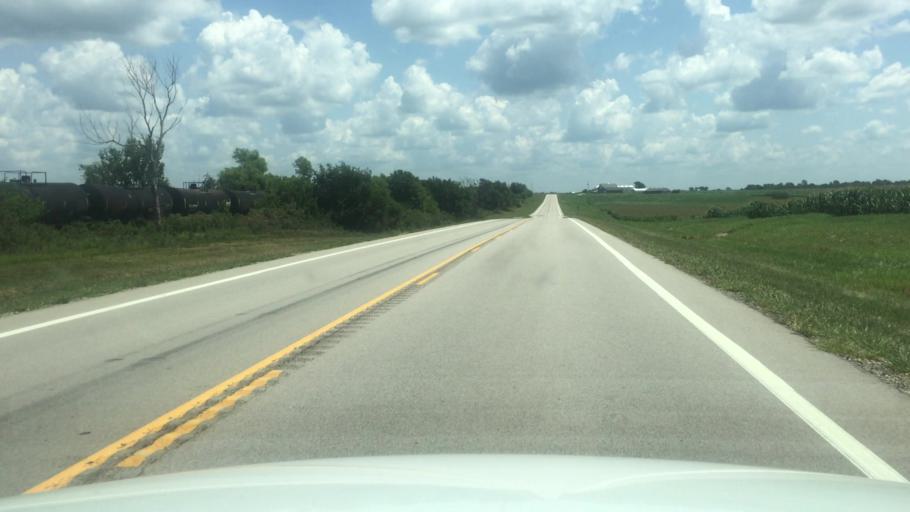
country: US
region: Kansas
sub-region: Brown County
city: Horton
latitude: 39.6560
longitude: -95.3717
